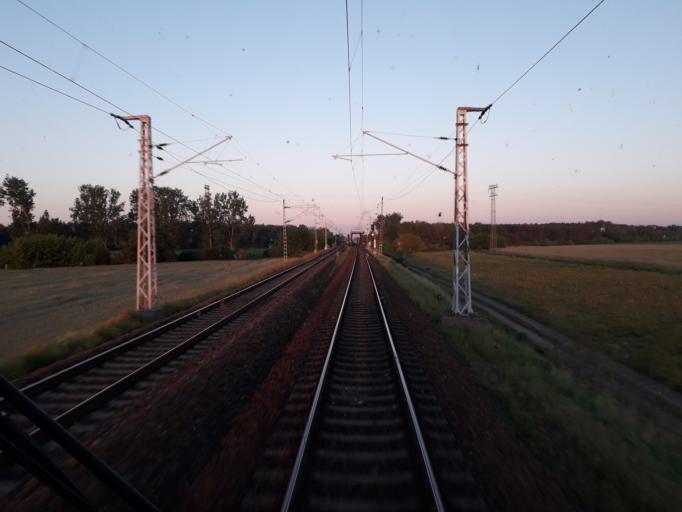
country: DE
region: Brandenburg
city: Falkensee
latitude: 52.6088
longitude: 13.0763
